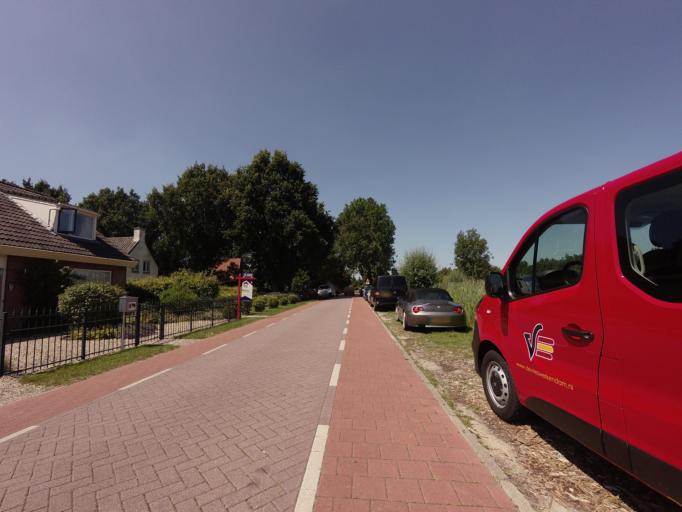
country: NL
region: Utrecht
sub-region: Stichtse Vecht
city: Maarssen
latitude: 52.1471
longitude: 5.0847
